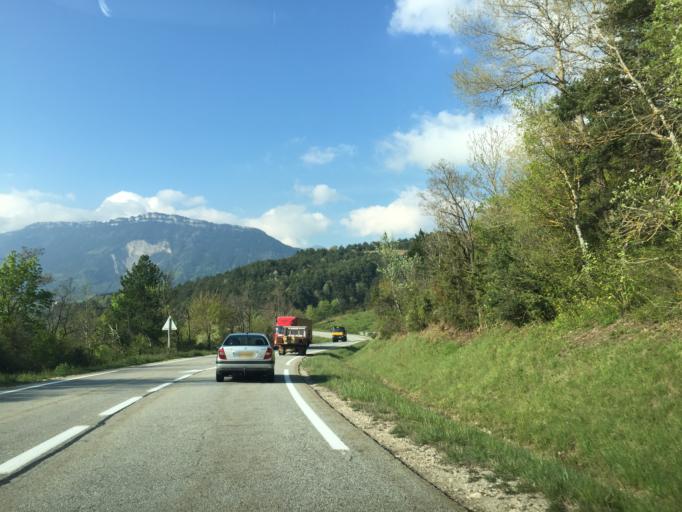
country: FR
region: Rhone-Alpes
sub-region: Departement de l'Isere
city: Mens
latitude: 44.8497
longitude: 5.6204
